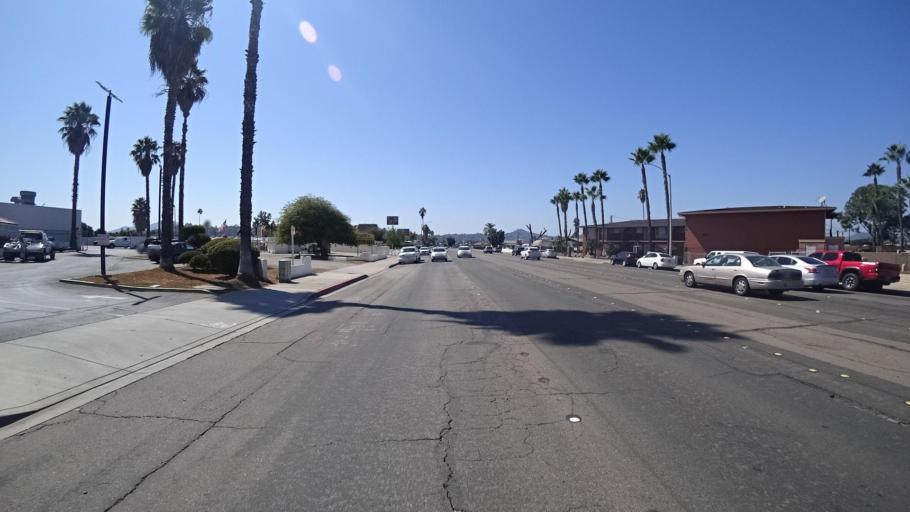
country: US
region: California
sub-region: San Diego County
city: Bostonia
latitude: 32.7987
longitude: -116.9321
